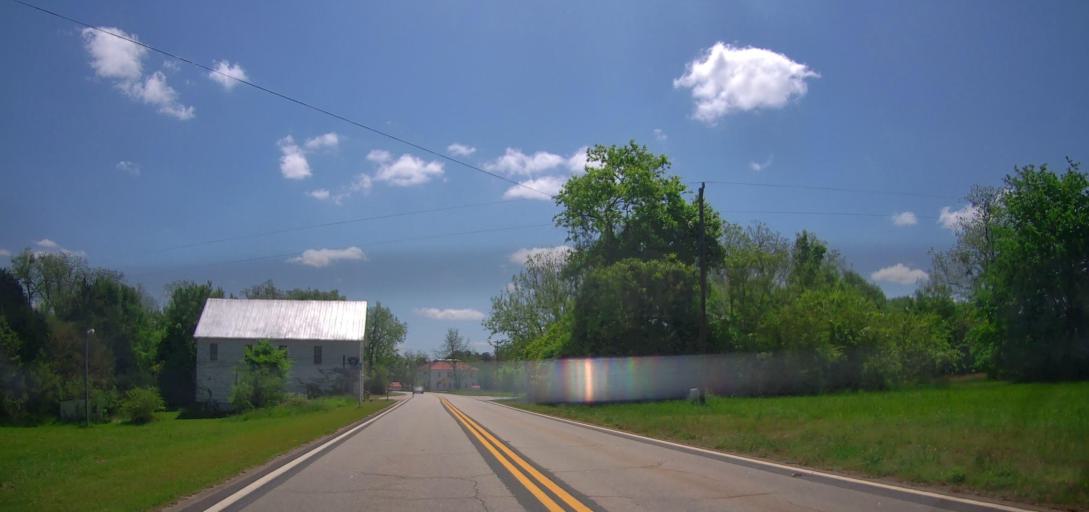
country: US
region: Georgia
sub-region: Jasper County
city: Monticello
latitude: 33.1787
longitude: -83.6403
